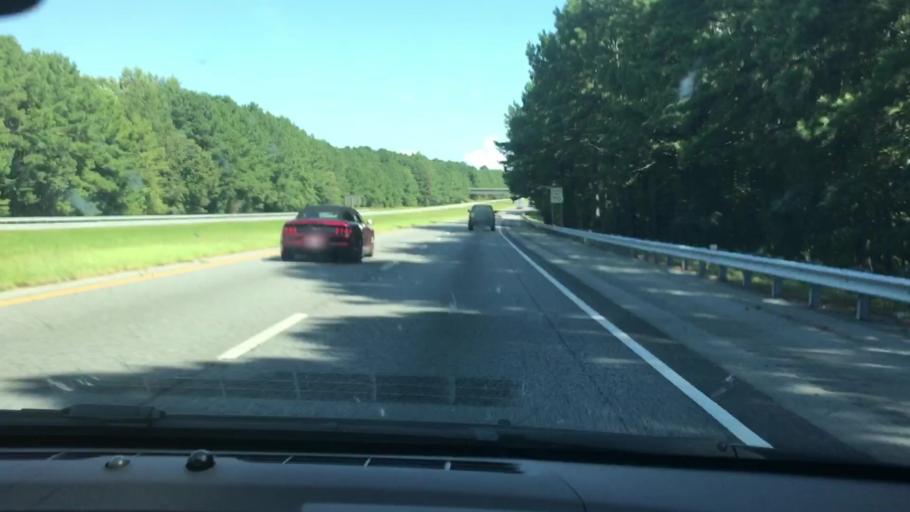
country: US
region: Alabama
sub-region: Russell County
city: Phenix City
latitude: 32.5782
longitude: -84.9614
